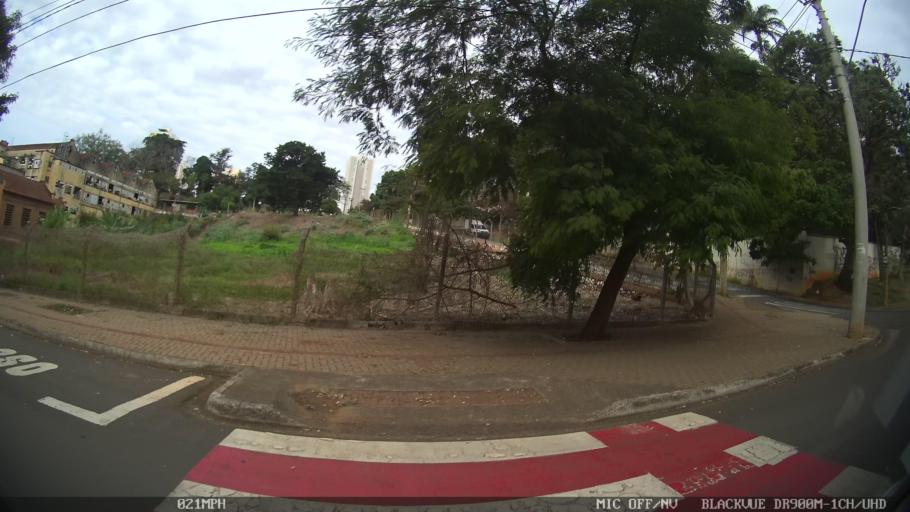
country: BR
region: Sao Paulo
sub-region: Piracicaba
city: Piracicaba
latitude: -22.7191
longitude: -47.6542
